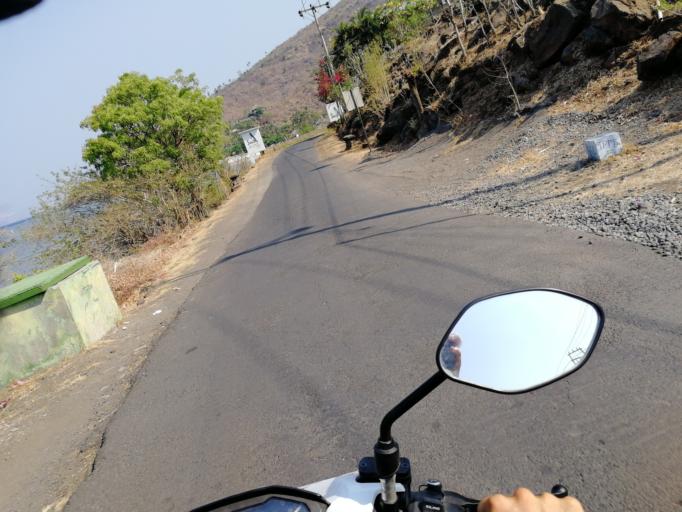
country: ID
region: Bali
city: Biaslantang Kaler
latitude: -8.3519
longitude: 115.6870
